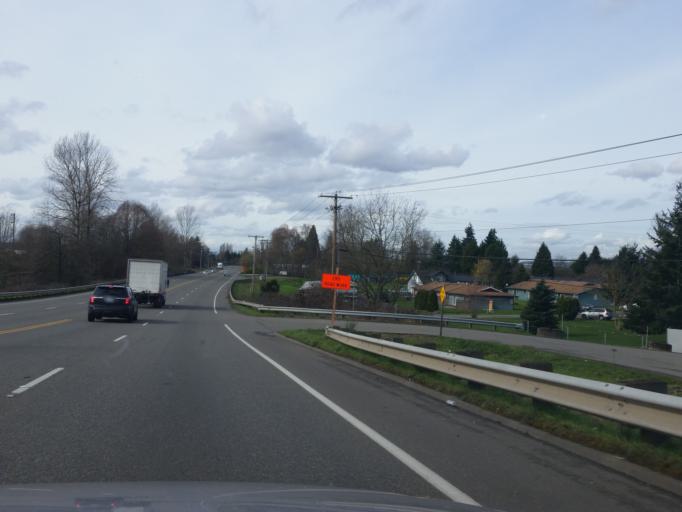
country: US
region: Washington
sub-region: Pierce County
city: Milton
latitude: 47.2186
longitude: -122.3147
